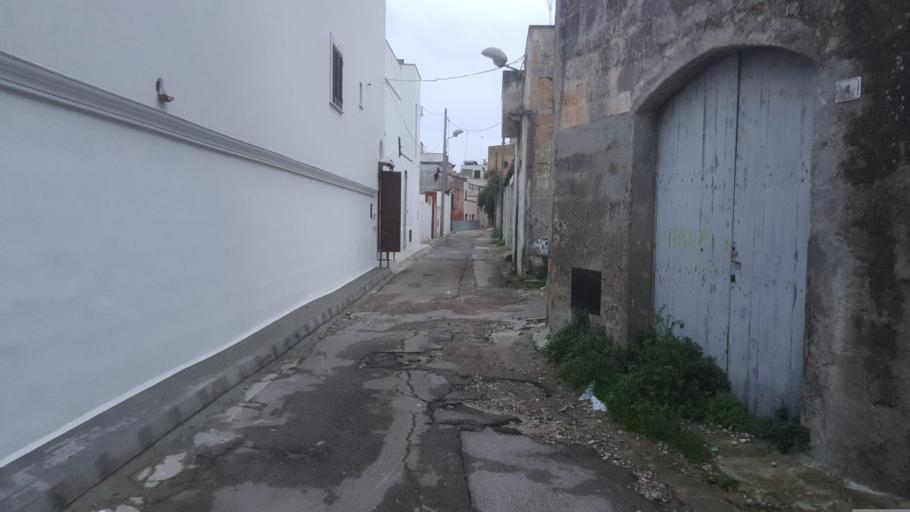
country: IT
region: Apulia
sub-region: Provincia di Lecce
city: Tricase
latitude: 39.9325
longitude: 18.3613
